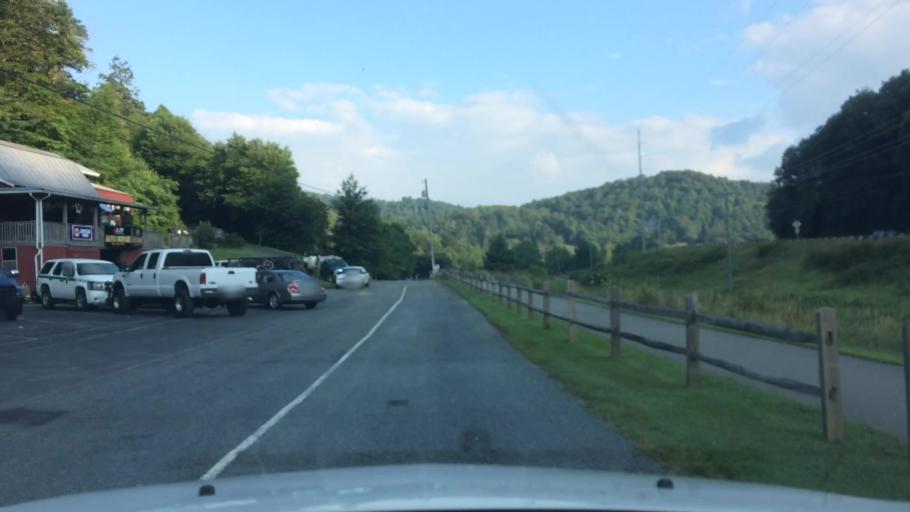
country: US
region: North Carolina
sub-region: Watauga County
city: Blowing Rock
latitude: 36.1638
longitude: -81.6446
